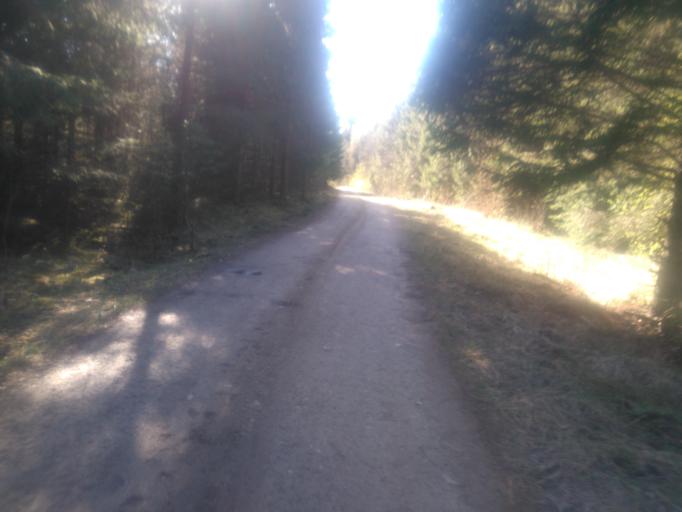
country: LV
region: Vecpiebalga
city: Vecpiebalga
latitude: 57.0065
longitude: 25.8514
